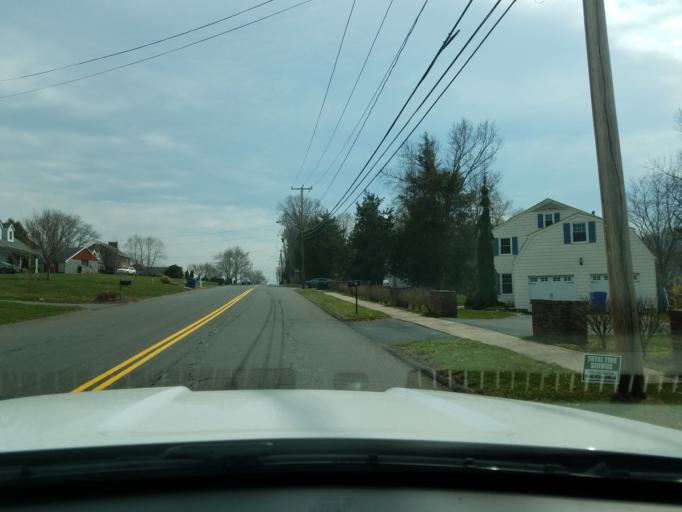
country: US
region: Connecticut
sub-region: Hartford County
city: Newington
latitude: 41.6858
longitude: -72.6917
